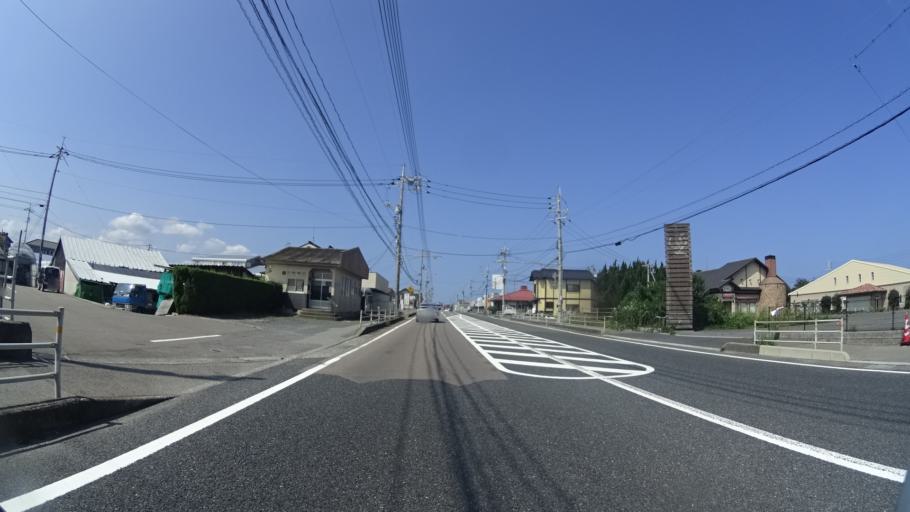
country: JP
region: Shimane
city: Masuda
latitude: 34.6898
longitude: 131.8148
